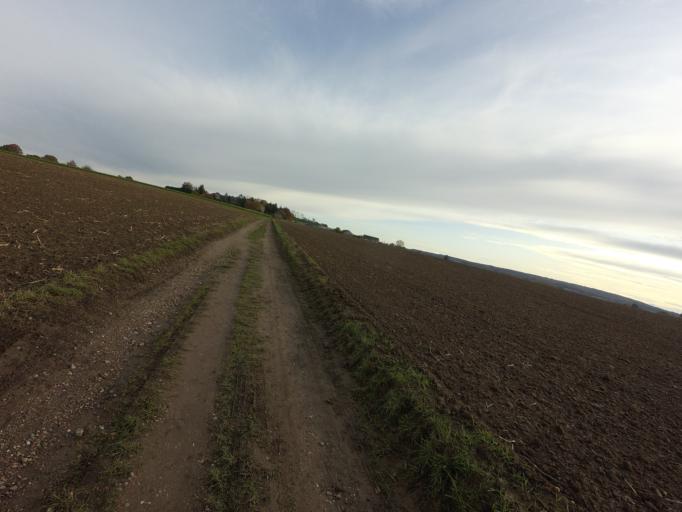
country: NL
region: Limburg
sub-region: Gemeente Voerendaal
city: Ubachsberg
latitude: 50.8067
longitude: 5.9285
